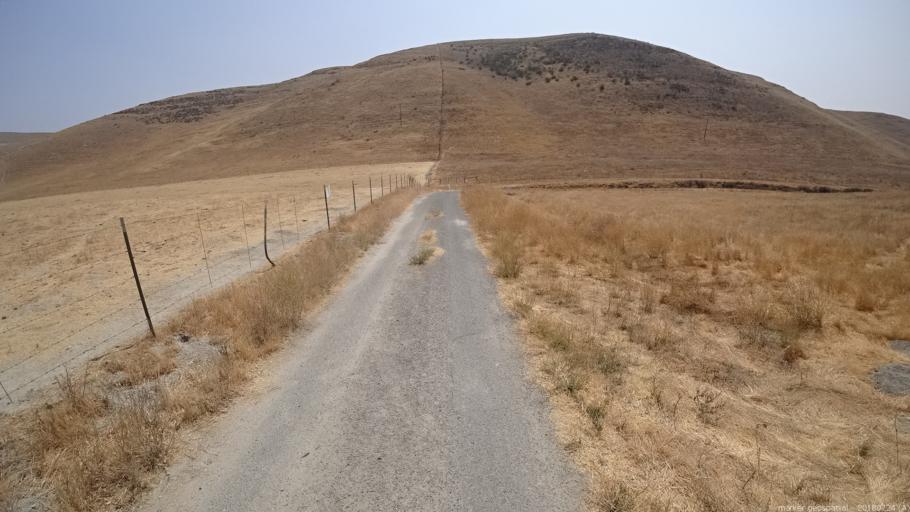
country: US
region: California
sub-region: Monterey County
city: King City
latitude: 36.1980
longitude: -120.9487
